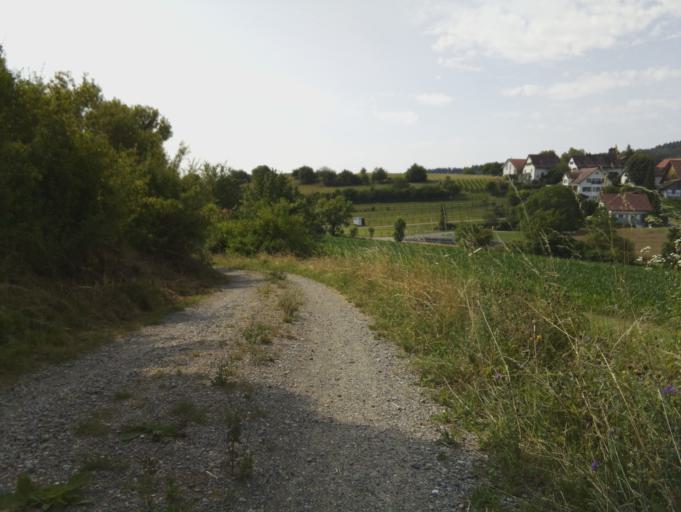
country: CH
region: Zurich
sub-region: Bezirk Andelfingen
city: Grossandelfingen
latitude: 47.5793
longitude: 8.6732
